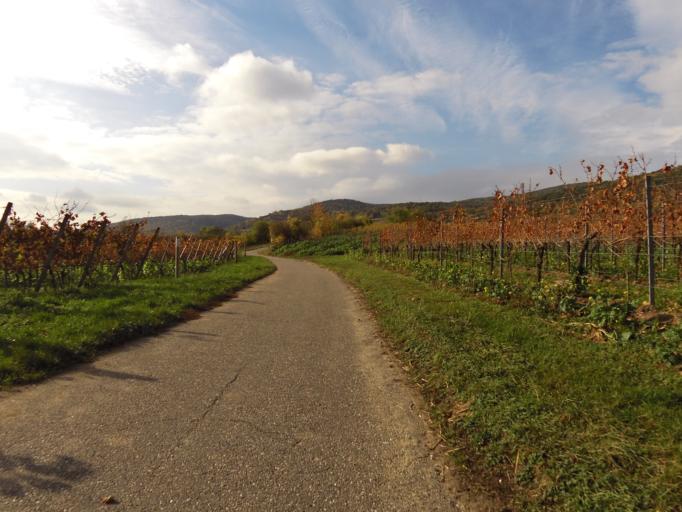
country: DE
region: Rheinland-Pfalz
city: Deidesheim
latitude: 49.4215
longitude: 8.1868
